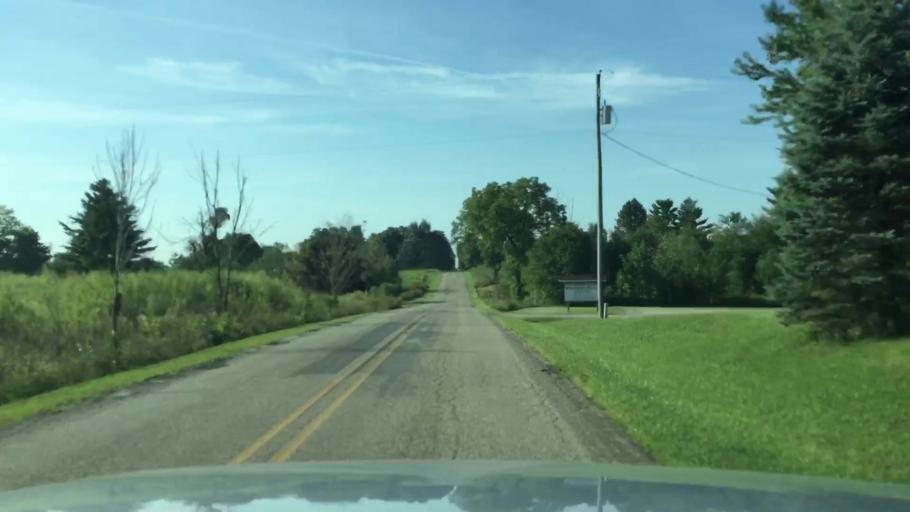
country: US
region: Michigan
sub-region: Lenawee County
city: Hudson
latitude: 41.8907
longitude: -84.4203
